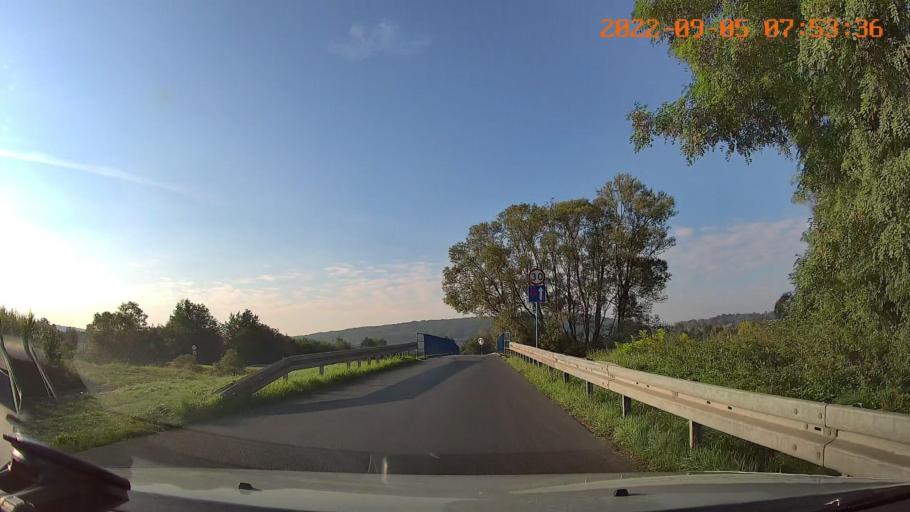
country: PL
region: Lesser Poland Voivodeship
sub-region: Powiat krakowski
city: Rzaska
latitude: 50.0783
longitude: 19.8485
